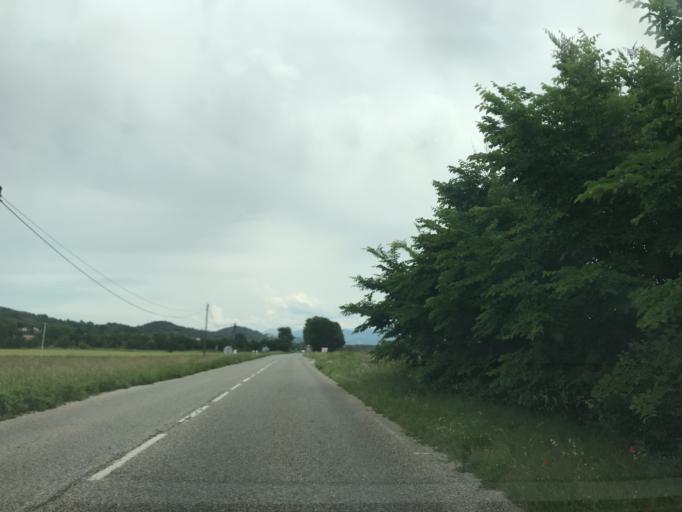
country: FR
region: Provence-Alpes-Cote d'Azur
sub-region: Departement des Alpes-de-Haute-Provence
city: Peyruis
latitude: 44.0352
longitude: 5.9469
